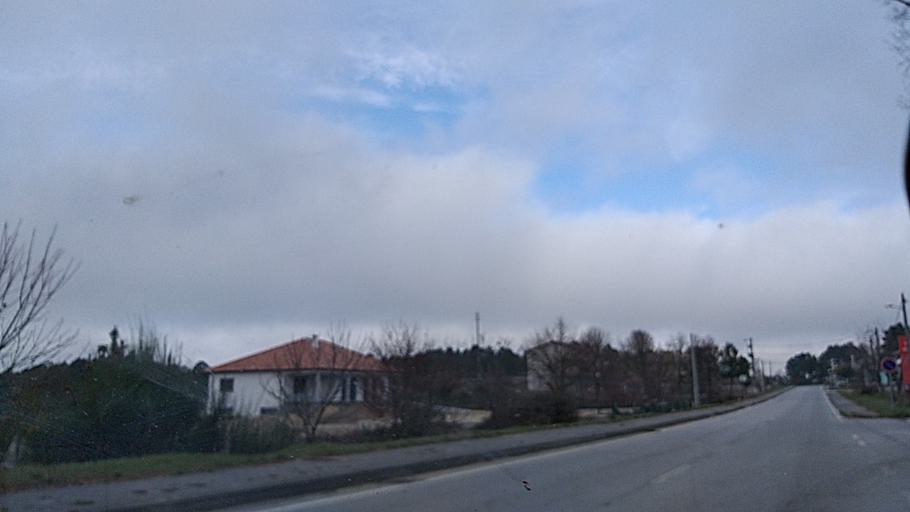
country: PT
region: Guarda
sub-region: Aguiar da Beira
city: Aguiar da Beira
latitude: 40.7413
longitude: -7.4961
